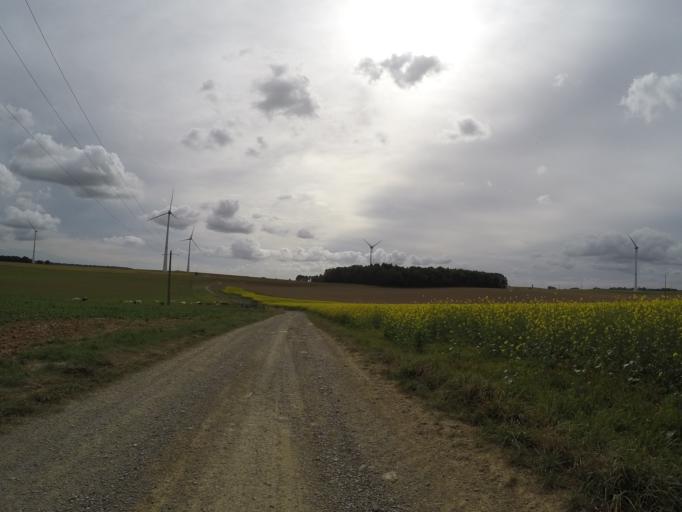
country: BE
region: Wallonia
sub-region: Province de Namur
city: Assesse
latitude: 50.3041
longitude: 4.9809
